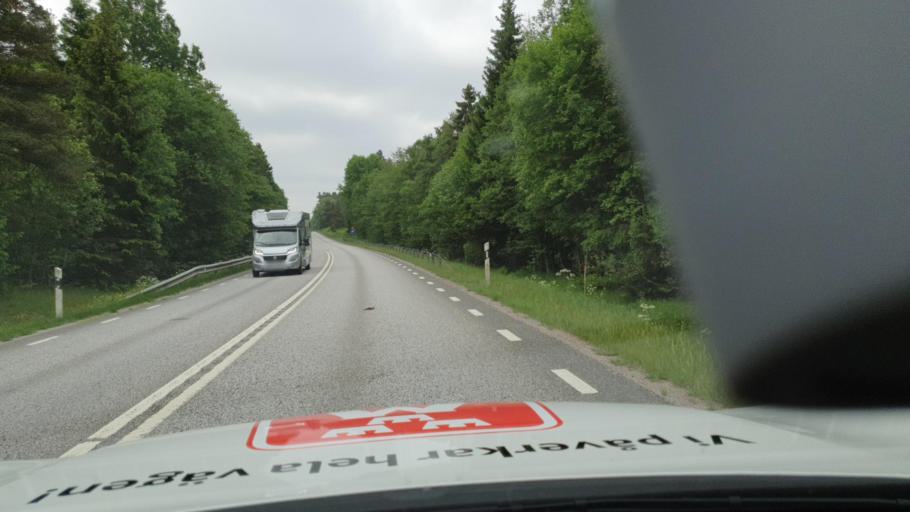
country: SE
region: Joenkoeping
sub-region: Mullsjo Kommun
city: Mullsjoe
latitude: 58.0176
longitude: 13.8275
